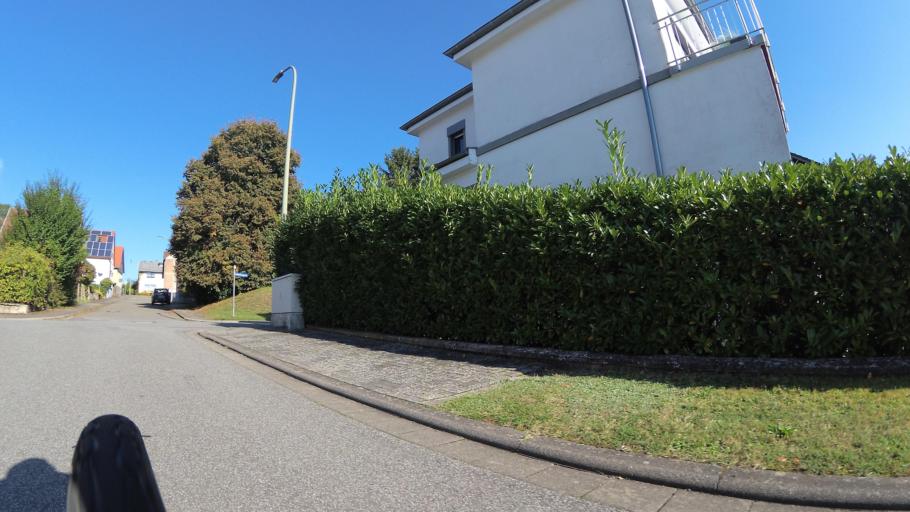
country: DE
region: Rheinland-Pfalz
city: Waldmohr
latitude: 49.3842
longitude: 7.3367
